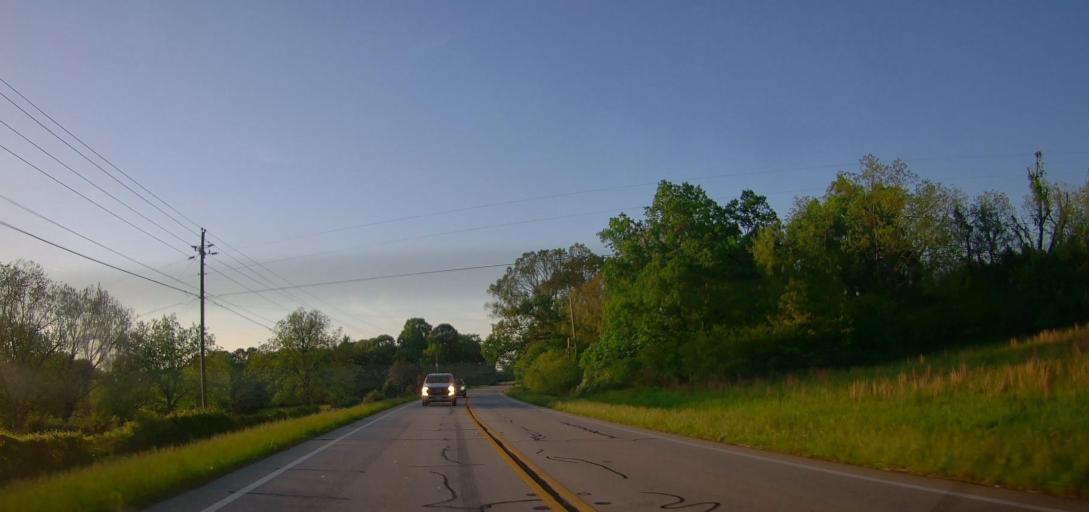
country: US
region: Georgia
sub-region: Newton County
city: Oakwood
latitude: 33.5258
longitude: -83.9520
